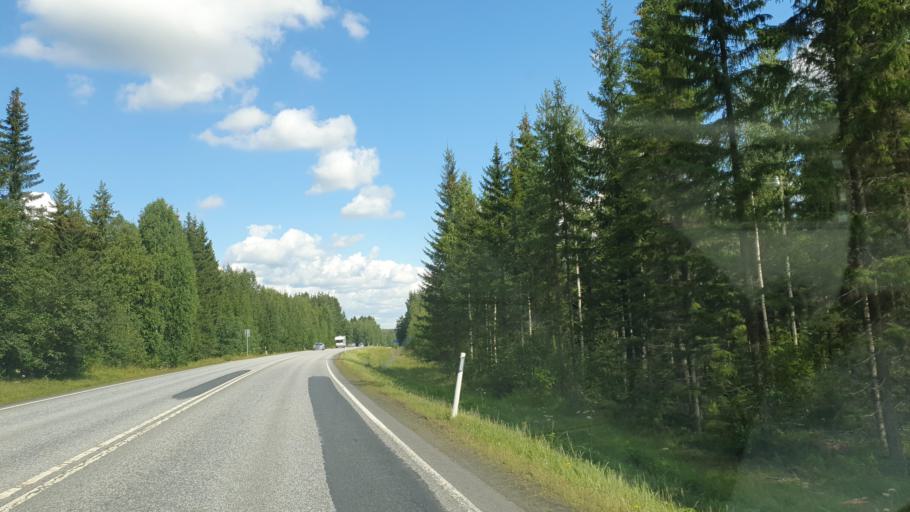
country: FI
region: Northern Savo
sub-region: Ylae-Savo
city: Sonkajaervi
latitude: 63.7484
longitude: 27.3843
